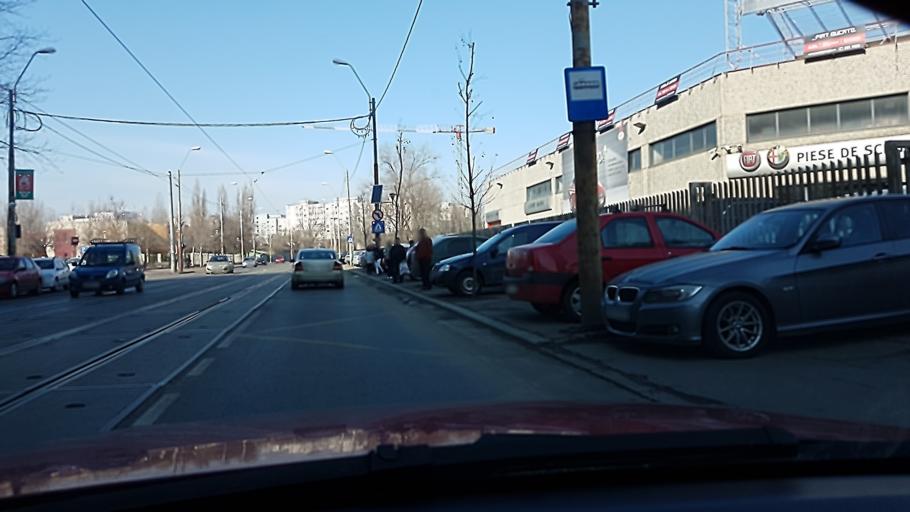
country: RO
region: Ilfov
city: Dobroesti
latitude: 44.4322
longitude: 26.1728
